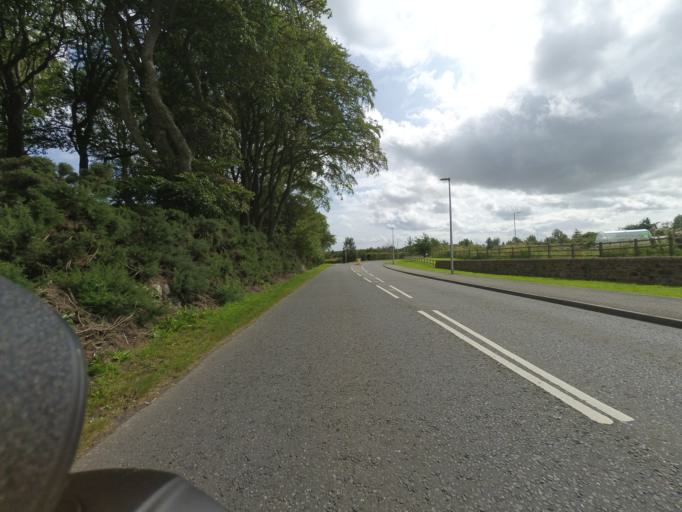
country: GB
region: Scotland
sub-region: Highland
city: Tain
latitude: 57.8040
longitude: -4.0457
